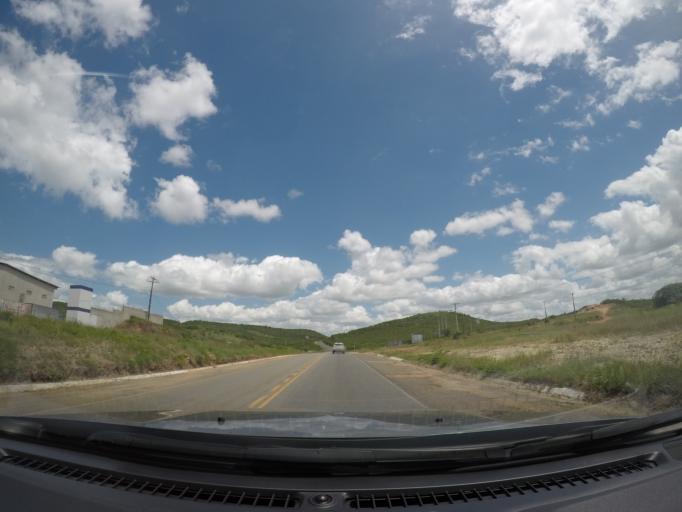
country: BR
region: Bahia
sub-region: Ipira
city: Ipira
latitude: -12.1689
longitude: -39.7316
